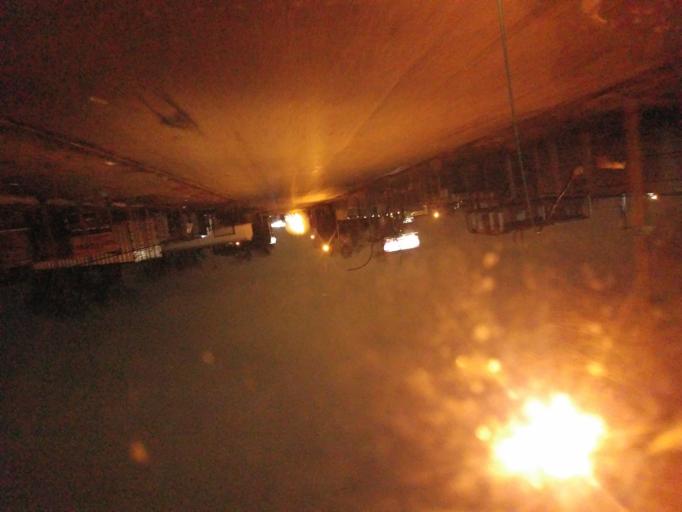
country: US
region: Illinois
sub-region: Madison County
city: Venice
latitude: 38.6569
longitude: -90.1941
